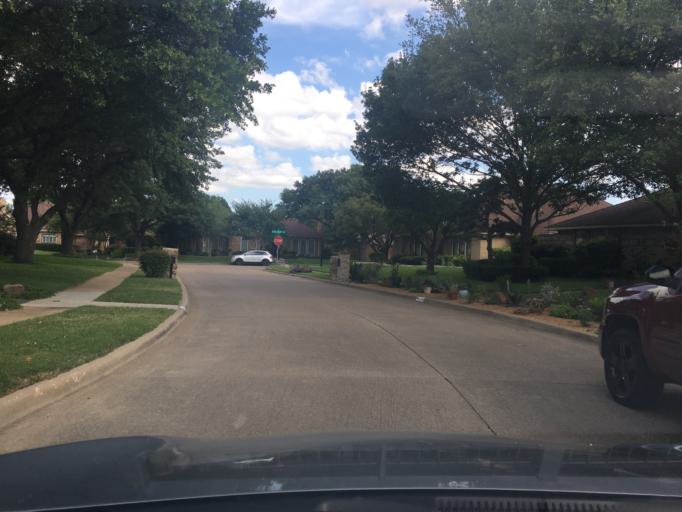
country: US
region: Texas
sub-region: Dallas County
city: Garland
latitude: 32.9358
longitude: -96.6774
